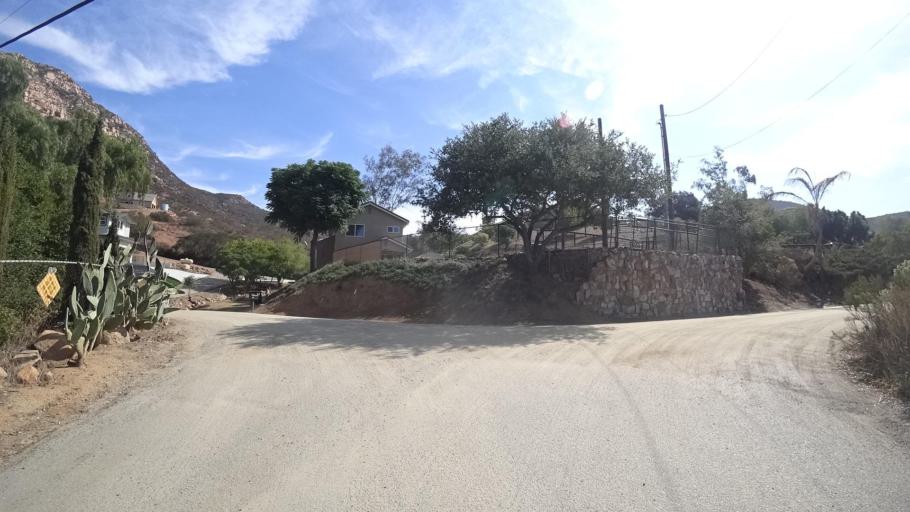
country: US
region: California
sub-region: San Diego County
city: Harbison Canyon
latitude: 32.8223
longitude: -116.8251
